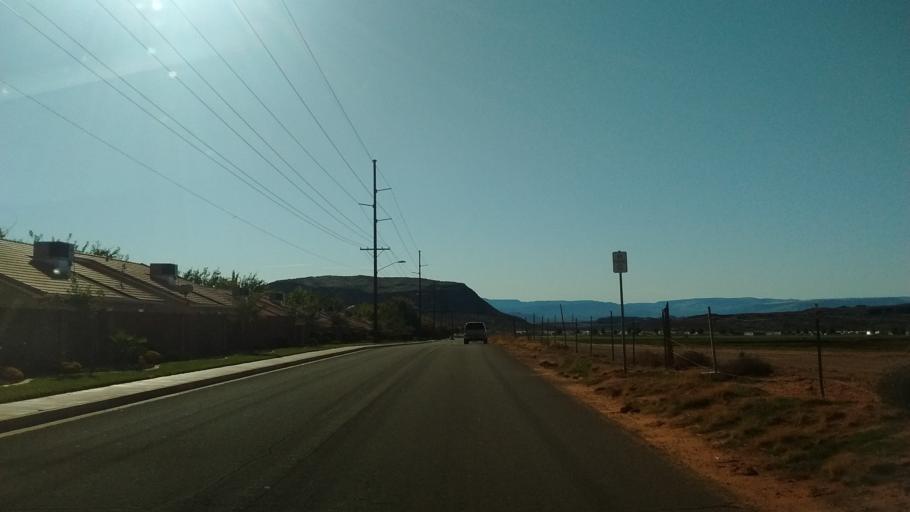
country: US
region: Utah
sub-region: Washington County
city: Washington
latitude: 37.1367
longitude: -113.4910
